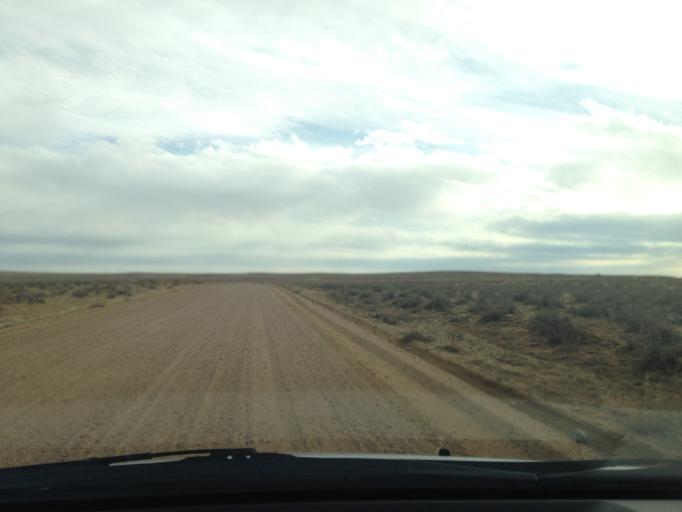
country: US
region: Colorado
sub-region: Weld County
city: Keenesburg
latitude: 40.2224
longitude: -104.2065
